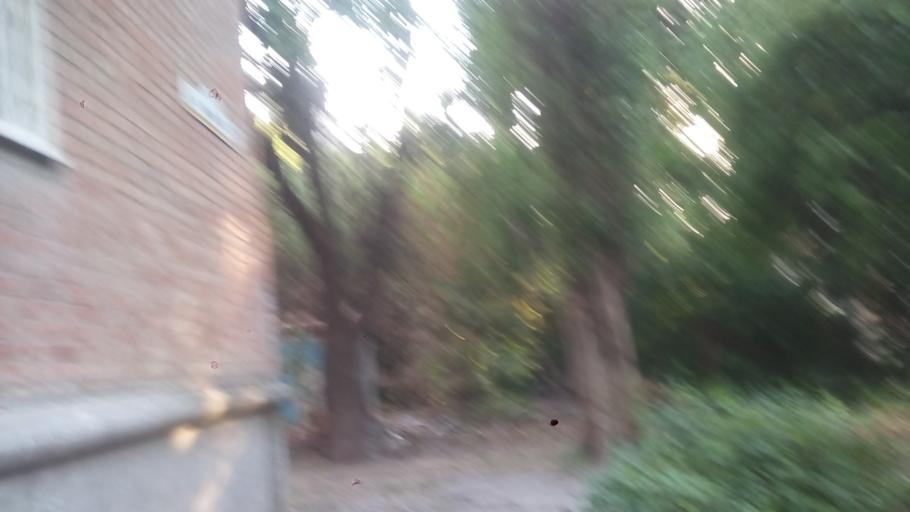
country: RU
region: Rostov
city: Rostov-na-Donu
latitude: 47.2460
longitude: 39.7453
